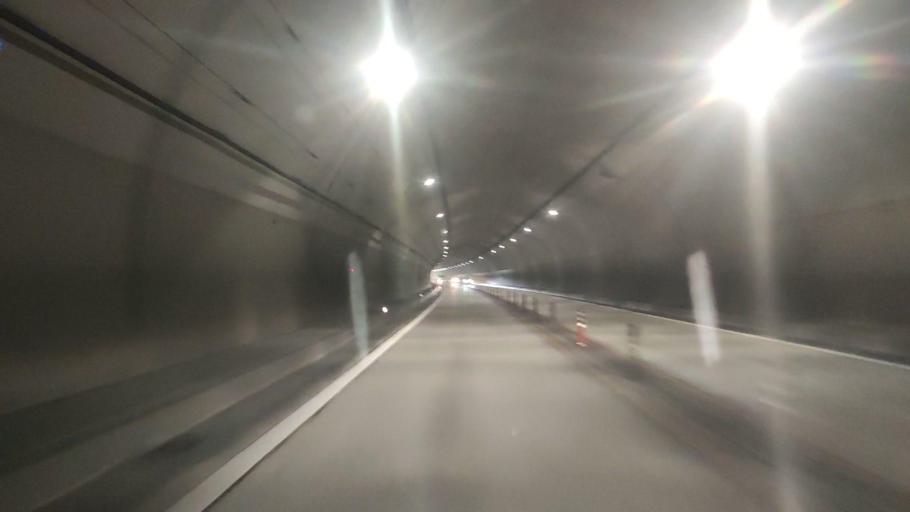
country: JP
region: Nagasaki
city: Shimabara
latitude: 32.7744
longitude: 130.3565
